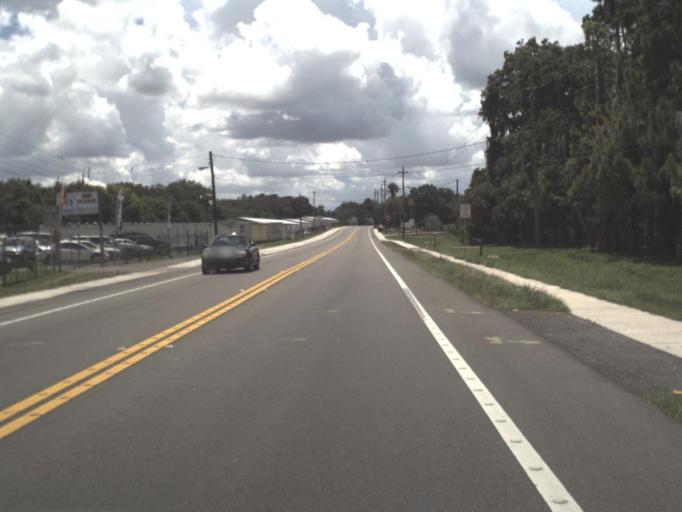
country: US
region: Florida
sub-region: Hillsborough County
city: Dover
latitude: 28.0054
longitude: -82.1768
